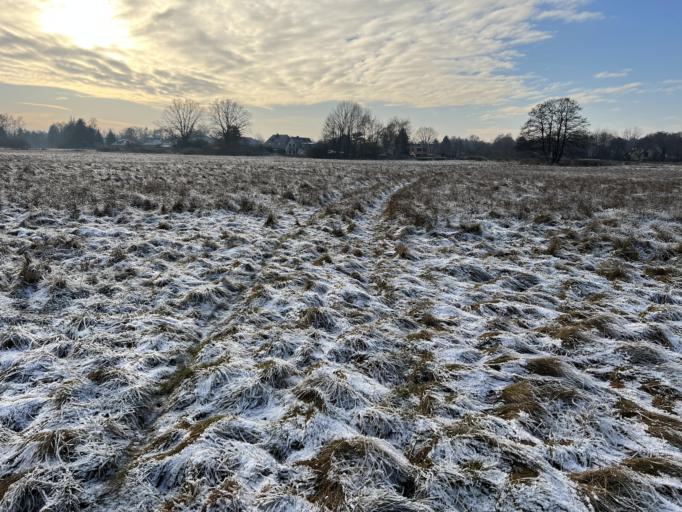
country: DE
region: Brandenburg
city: Konigs Wusterhausen
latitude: 52.2837
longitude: 13.6453
